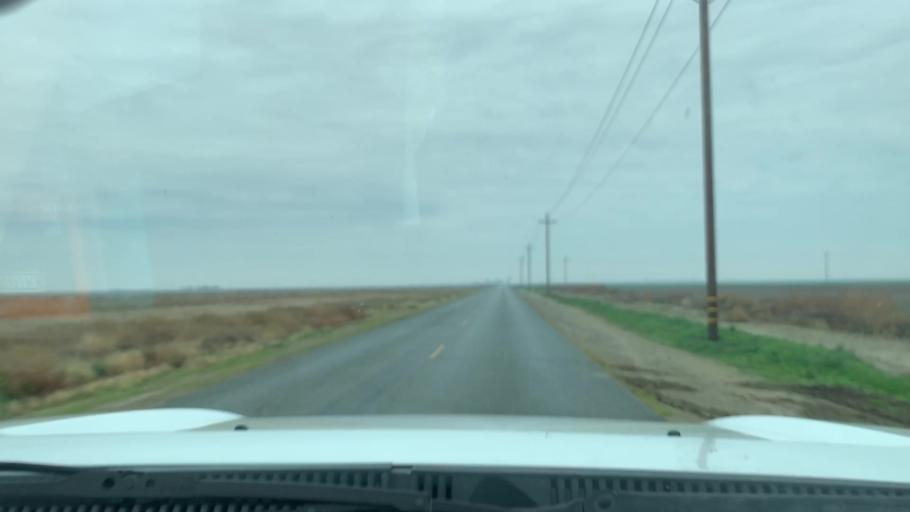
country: US
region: California
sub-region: Tulare County
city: Alpaugh
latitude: 35.7610
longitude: -119.4486
